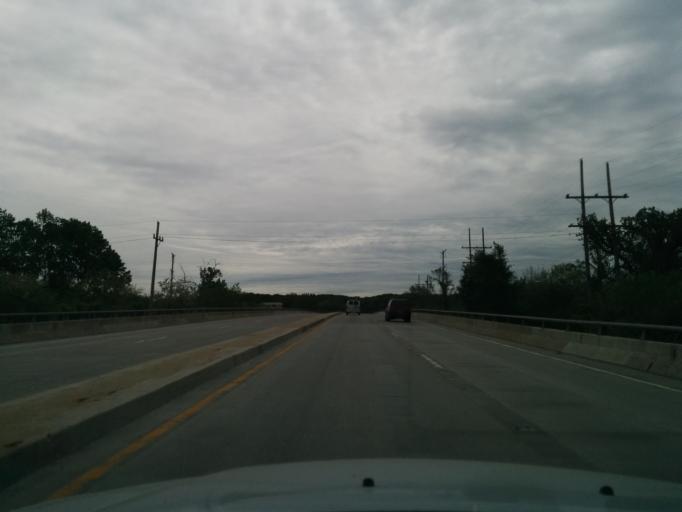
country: US
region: Illinois
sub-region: Cook County
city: Willow Springs
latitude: 41.7358
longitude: -87.8818
